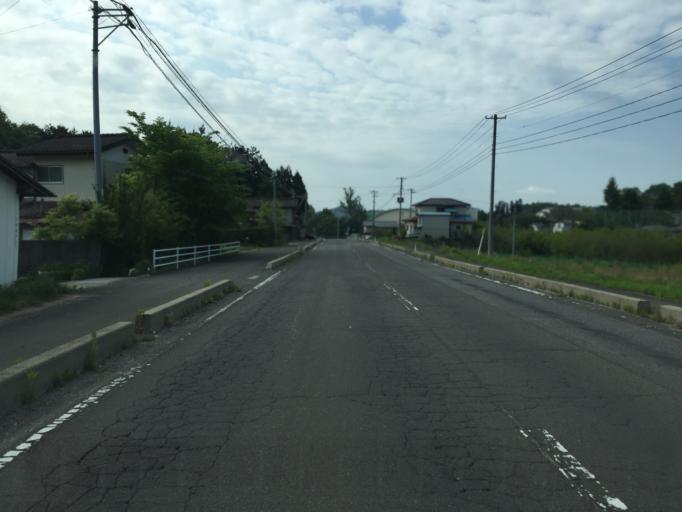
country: JP
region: Fukushima
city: Fukushima-shi
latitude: 37.6622
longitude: 140.5317
